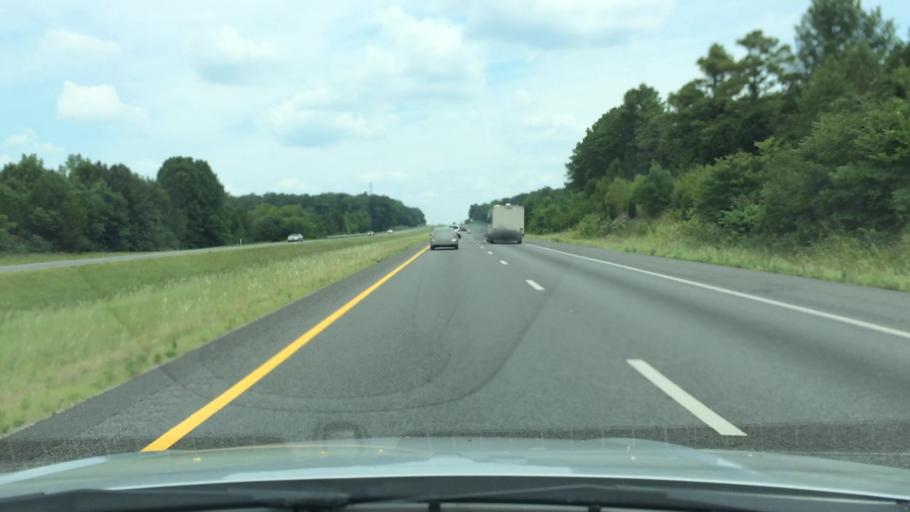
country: US
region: Tennessee
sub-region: Maury County
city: Spring Hill
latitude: 35.6741
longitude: -86.8898
